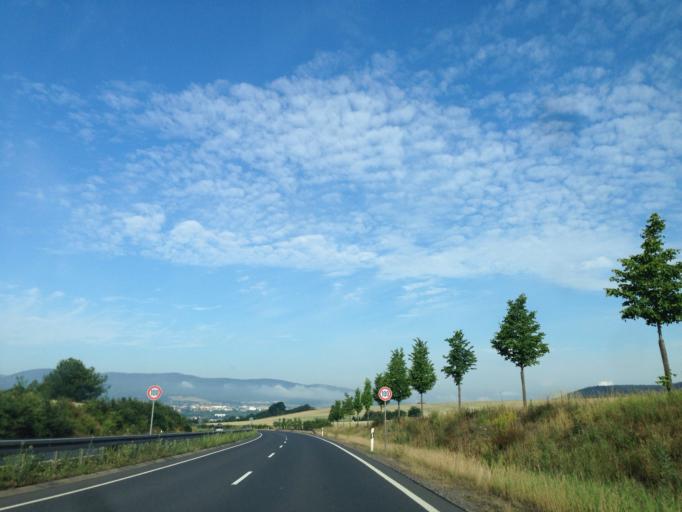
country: DE
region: Thuringia
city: Unterwellenborn
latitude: 50.6608
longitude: 11.4040
